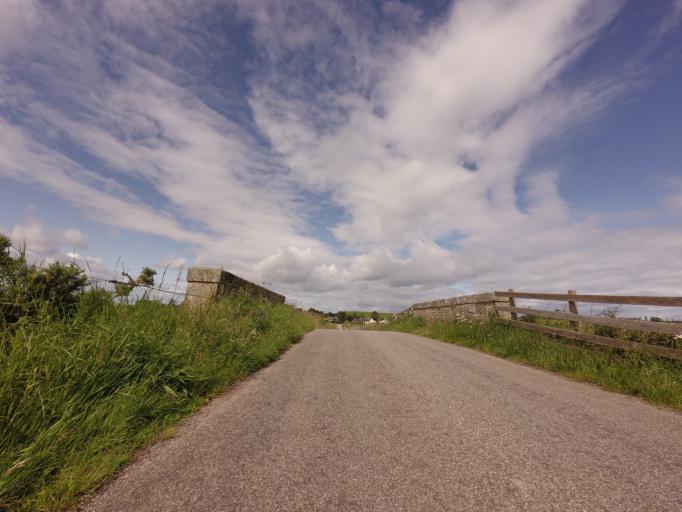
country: GB
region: Scotland
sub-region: Moray
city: Burghead
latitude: 57.6541
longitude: -3.4729
